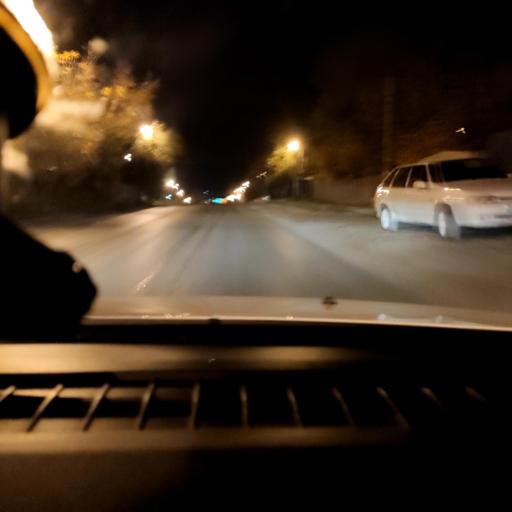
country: RU
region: Samara
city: Samara
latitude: 53.1834
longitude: 50.1544
